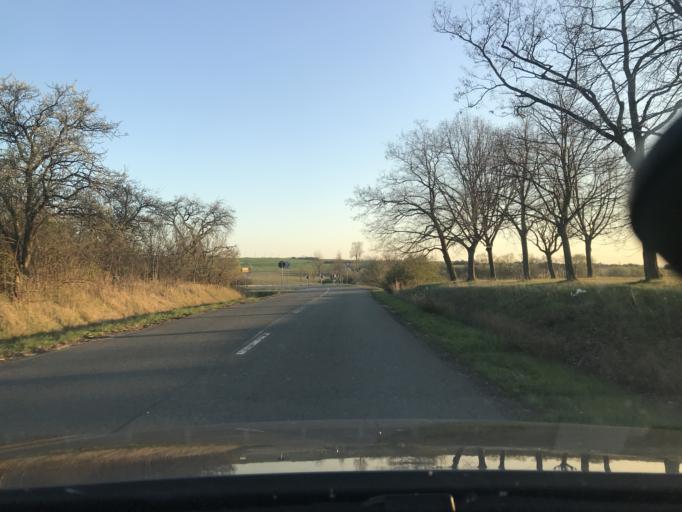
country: DE
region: Thuringia
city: Sollstedt
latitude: 51.2700
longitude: 10.5096
